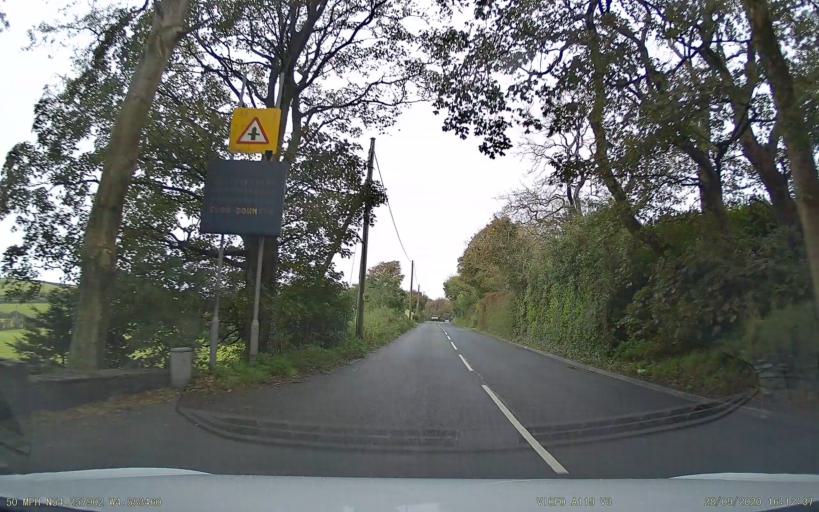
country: IM
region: Douglas
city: Douglas
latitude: 54.2579
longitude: -4.5835
